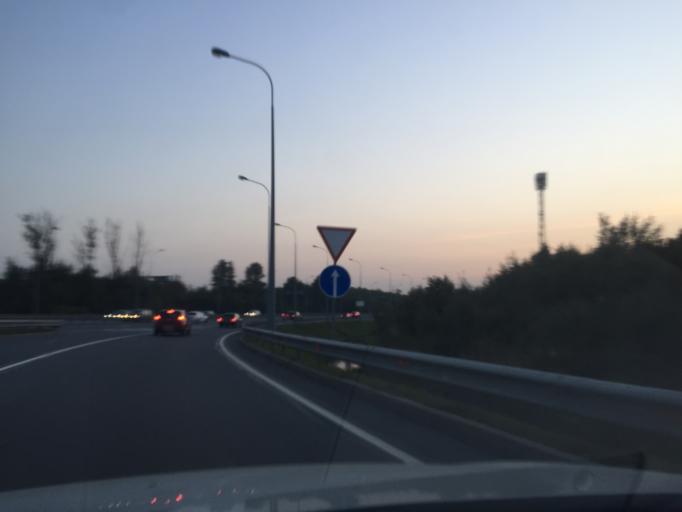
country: RU
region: St.-Petersburg
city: Krasnogvargeisky
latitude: 59.9893
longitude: 30.4796
